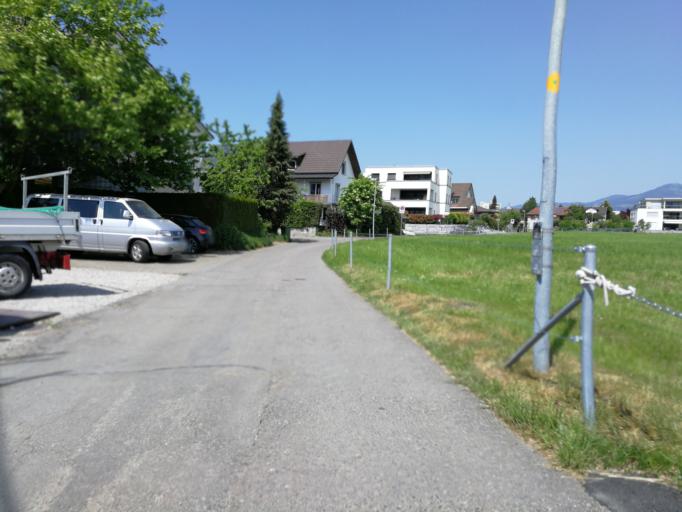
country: CH
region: Saint Gallen
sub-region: Wahlkreis See-Gaster
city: Jona
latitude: 47.2179
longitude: 8.8333
